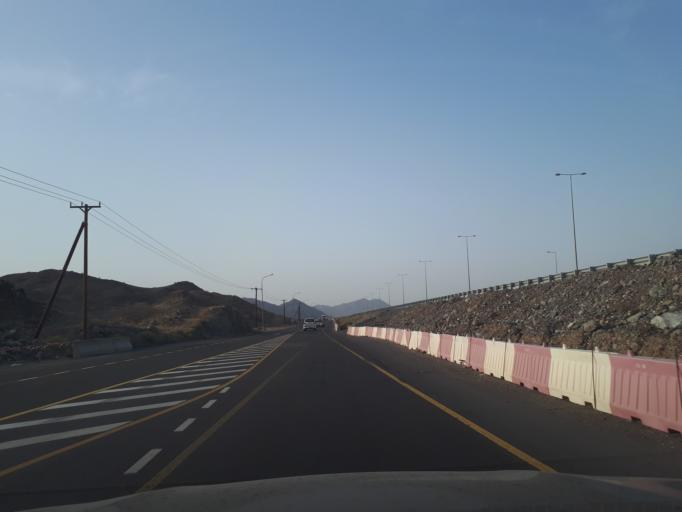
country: OM
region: Muhafazat ad Dakhiliyah
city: Sufalat Sama'il
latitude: 23.2838
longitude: 58.1080
